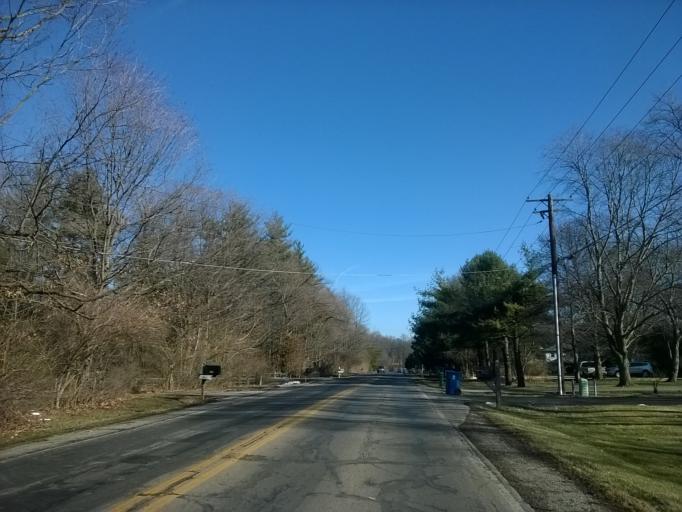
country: US
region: Indiana
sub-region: Marion County
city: Meridian Hills
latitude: 39.8976
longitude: -86.1699
